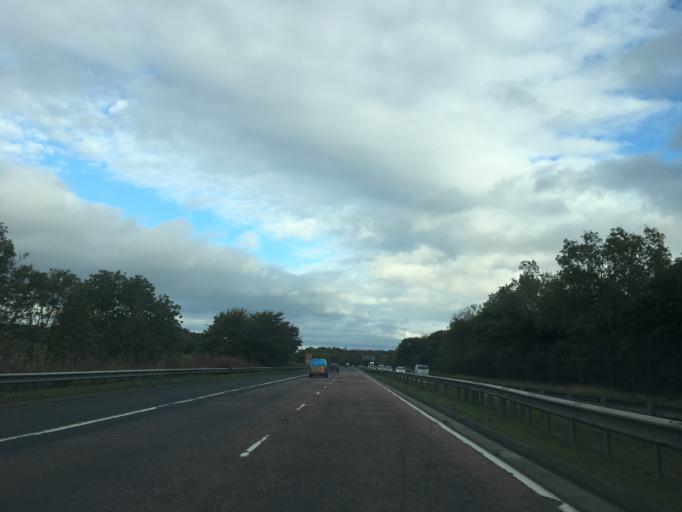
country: GB
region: Scotland
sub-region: Edinburgh
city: Queensferry
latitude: 55.9799
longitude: -3.3638
